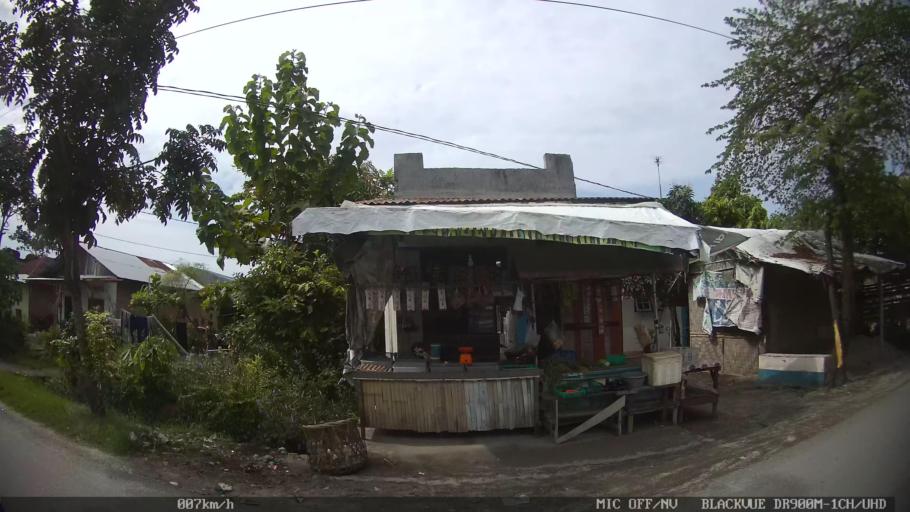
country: ID
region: North Sumatra
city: Percut
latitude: 3.6198
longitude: 98.7961
